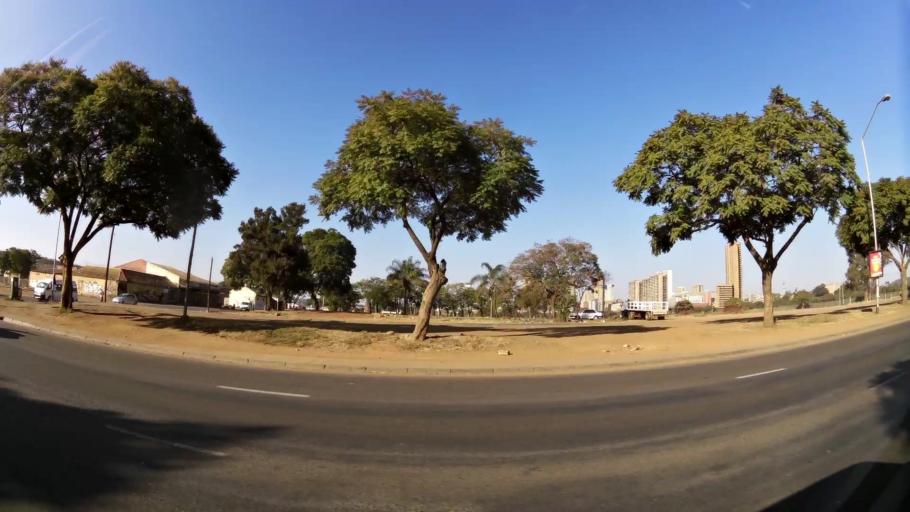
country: ZA
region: Gauteng
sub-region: City of Tshwane Metropolitan Municipality
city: Pretoria
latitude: -25.7420
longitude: 28.1730
